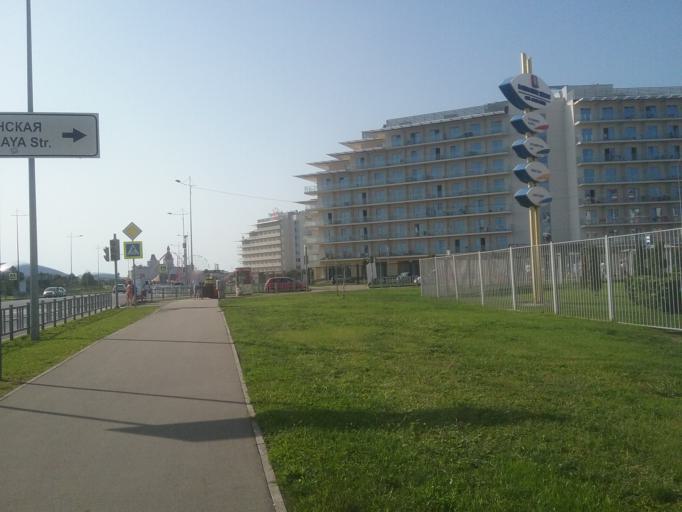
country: RU
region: Krasnodarskiy
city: Adler
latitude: 43.4005
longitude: 39.9779
